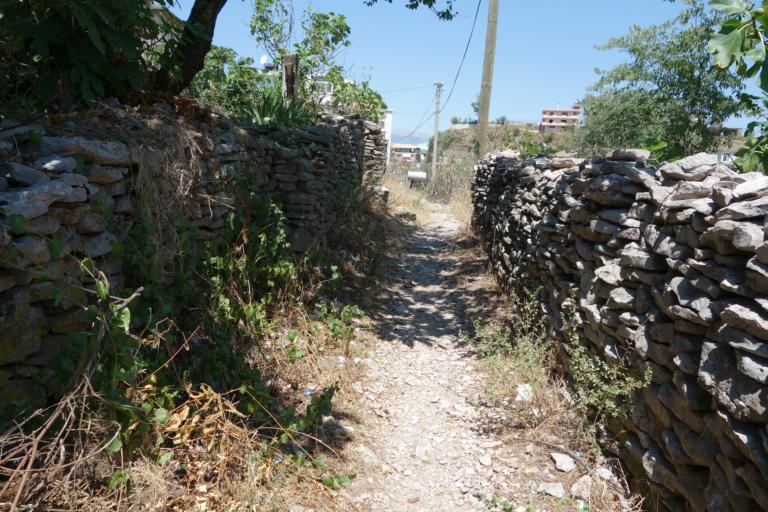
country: AL
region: Gjirokaster
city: Gjirokaster
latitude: 40.0795
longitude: 20.1329
